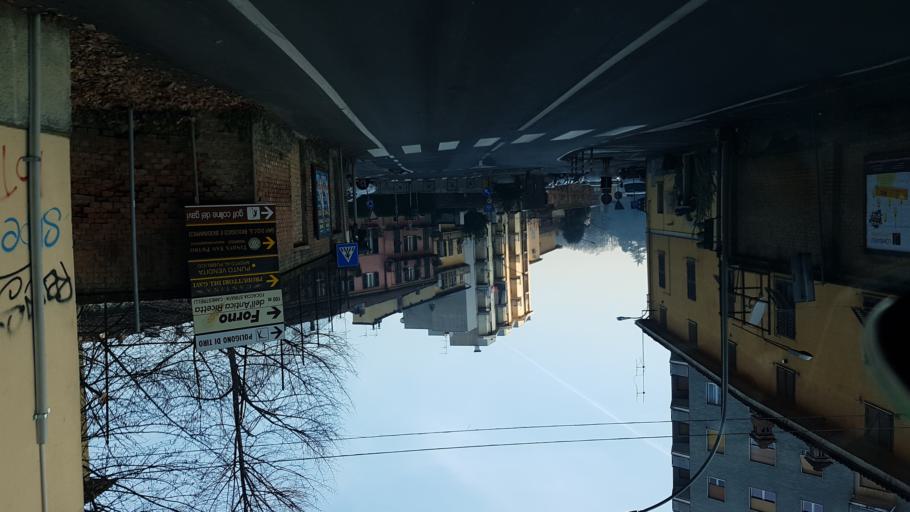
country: IT
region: Piedmont
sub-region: Provincia di Alessandria
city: Novi Ligure
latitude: 44.7578
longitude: 8.7847
